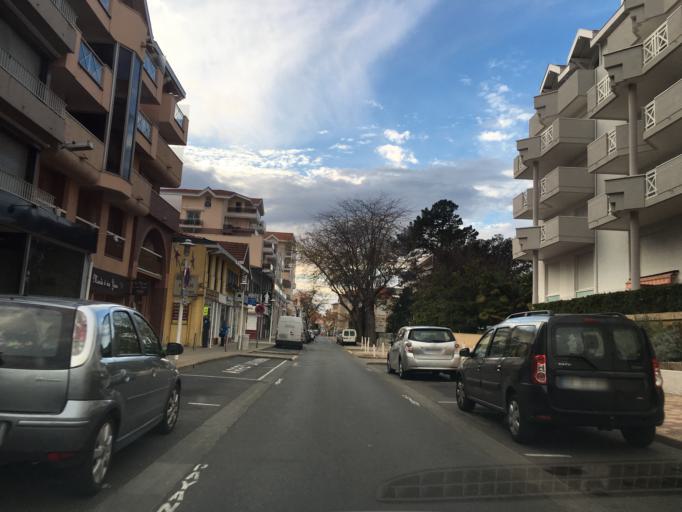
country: FR
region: Aquitaine
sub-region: Departement de la Gironde
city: Arcachon
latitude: 44.6627
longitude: -1.1649
